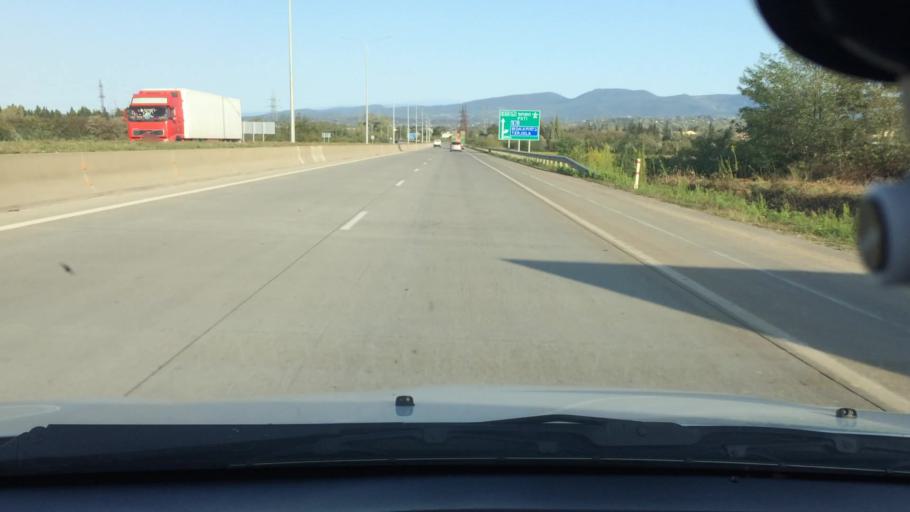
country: GE
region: Imereti
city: Zestap'oni
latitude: 42.1504
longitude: 42.9610
